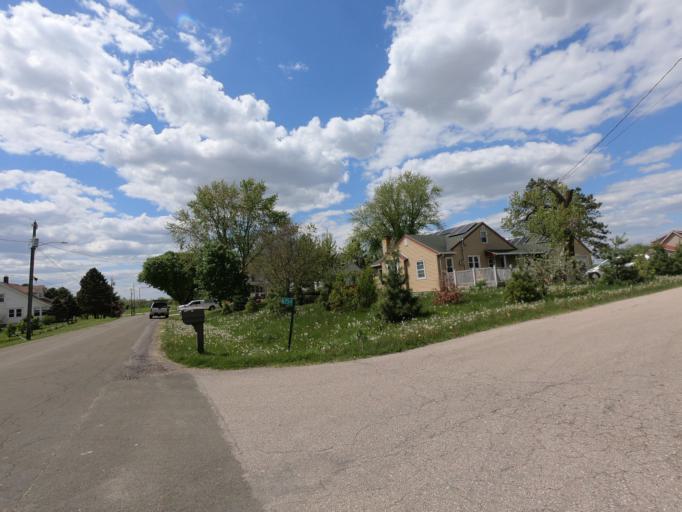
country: US
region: Wisconsin
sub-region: Dane County
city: Belleville
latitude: 42.9120
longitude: -89.5152
